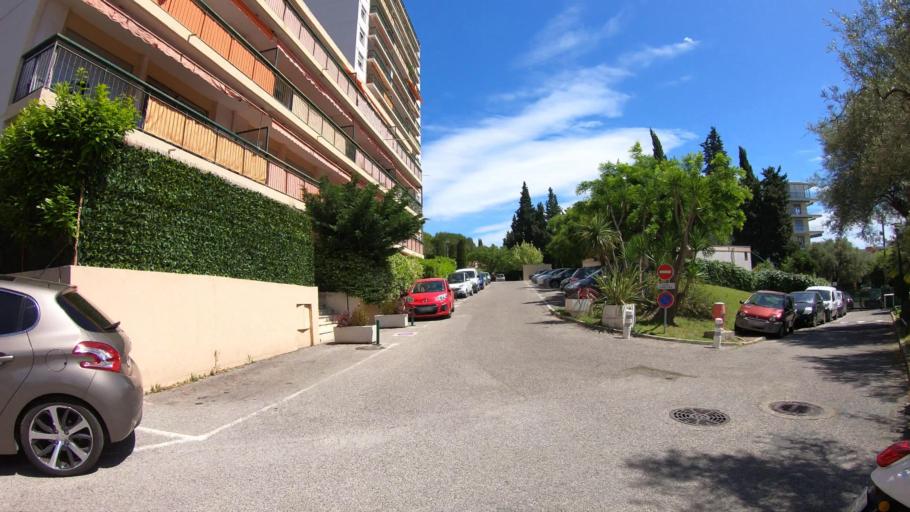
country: FR
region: Provence-Alpes-Cote d'Azur
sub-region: Departement des Alpes-Maritimes
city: Antibes
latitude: 43.5823
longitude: 7.0954
